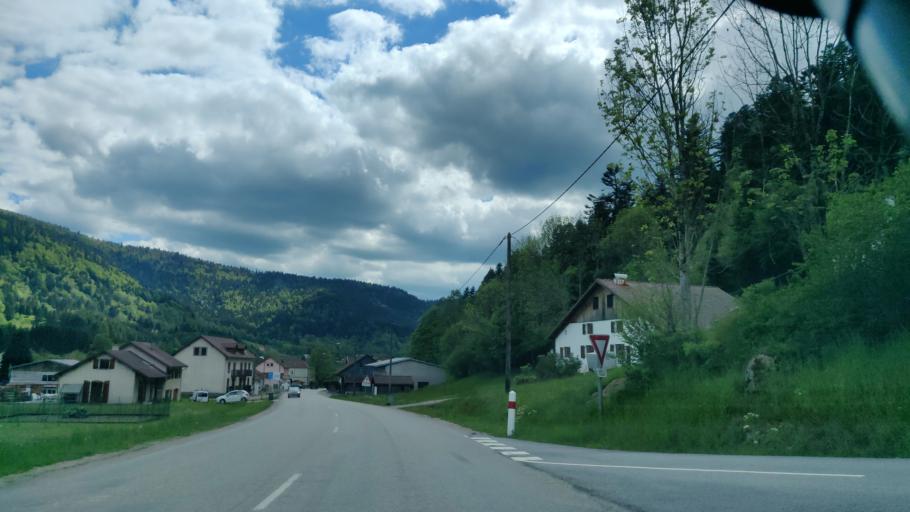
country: FR
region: Lorraine
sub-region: Departement des Vosges
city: Xonrupt-Longemer
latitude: 48.0133
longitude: 6.9415
